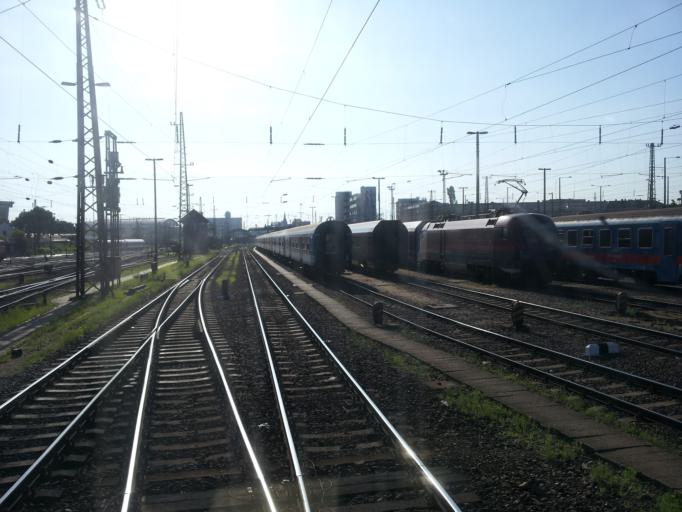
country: HU
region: Budapest
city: Budapest VII. keruelet
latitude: 47.5004
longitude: 19.0914
